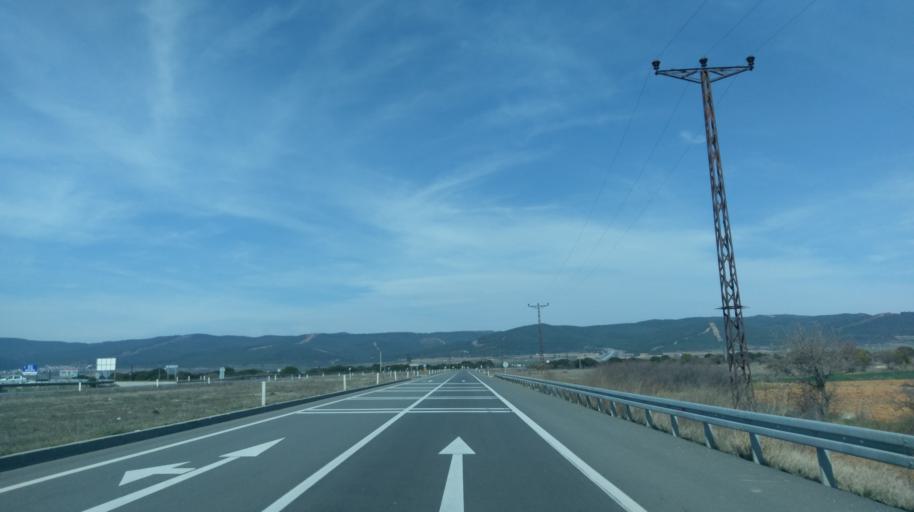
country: TR
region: Canakkale
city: Evrese
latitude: 40.6650
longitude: 26.8058
